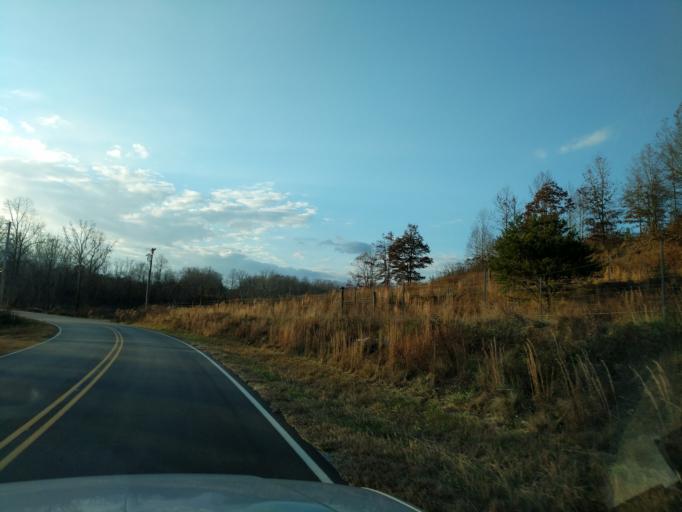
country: US
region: North Carolina
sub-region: Rutherford County
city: Rutherfordton
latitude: 35.2689
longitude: -82.0428
